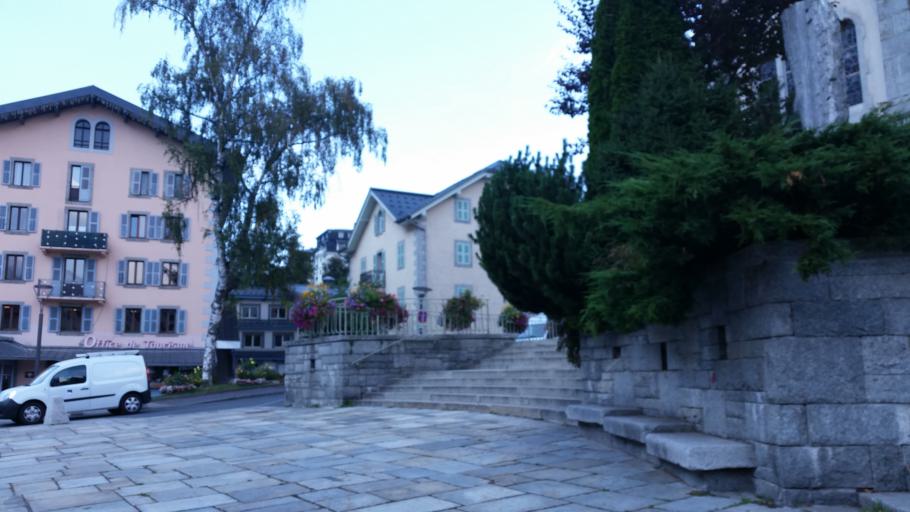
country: FR
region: Rhone-Alpes
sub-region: Departement de la Haute-Savoie
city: Chamonix-Mont-Blanc
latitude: 45.9238
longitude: 6.8685
